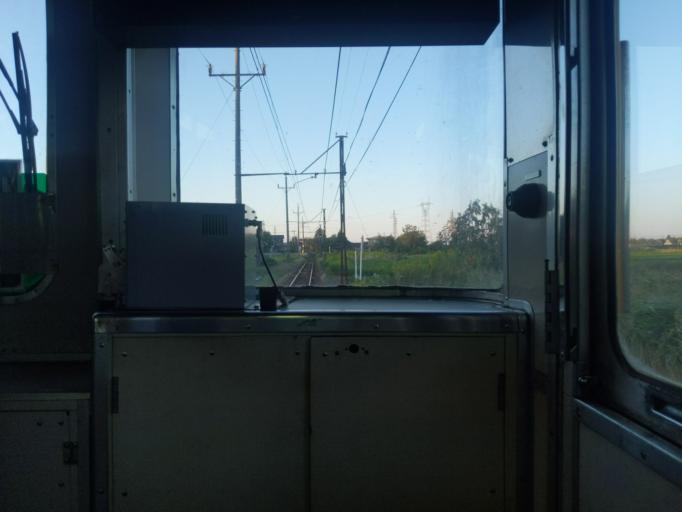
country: JP
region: Toyama
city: Kamiichi
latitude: 36.6958
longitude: 137.3185
